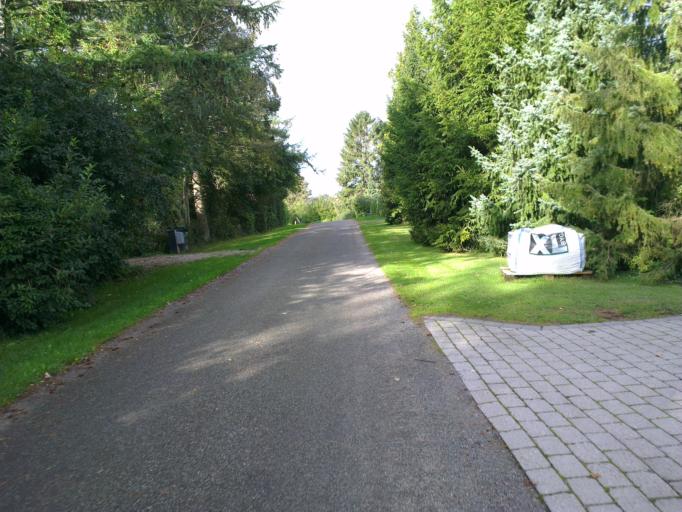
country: DK
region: Capital Region
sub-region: Frederikssund Kommune
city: Jaegerspris
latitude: 55.8304
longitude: 11.9626
